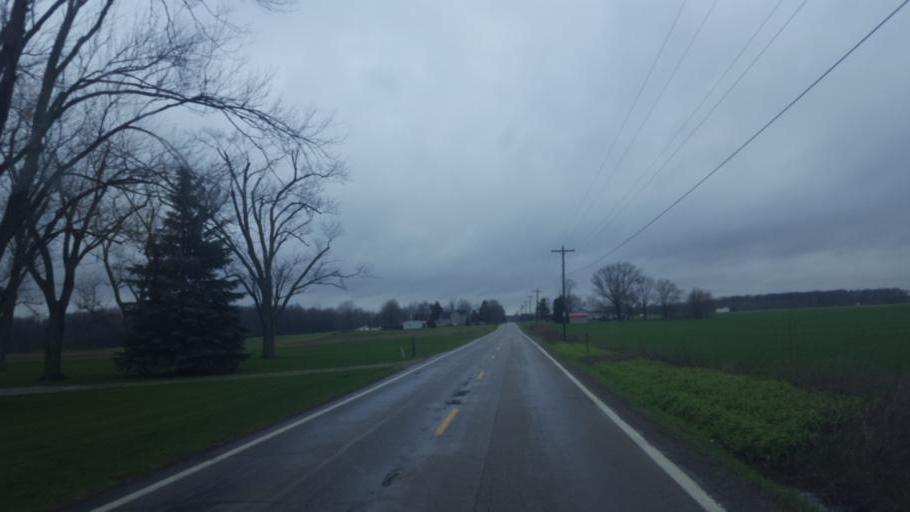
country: US
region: Ohio
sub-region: Morrow County
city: Cardington
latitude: 40.4877
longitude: -82.8587
